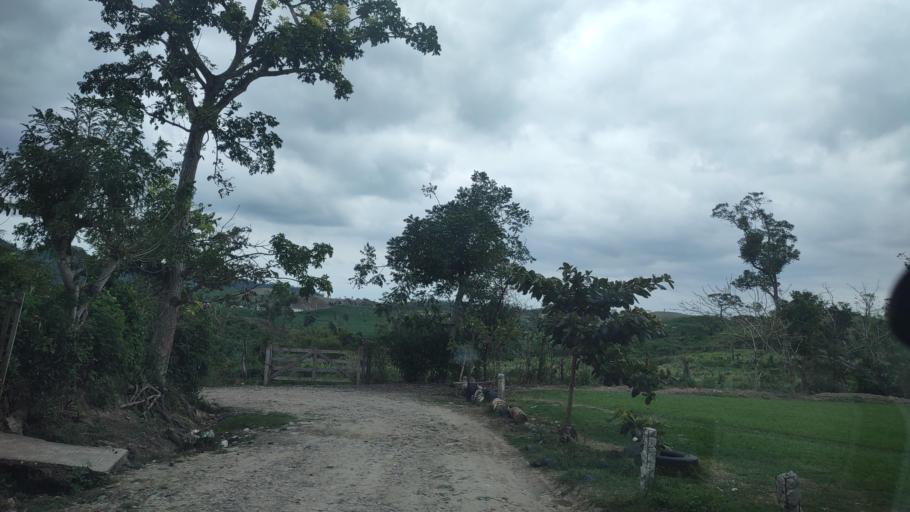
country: MX
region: Veracruz
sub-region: Papantla
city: Polutla
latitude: 20.4644
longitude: -97.2559
